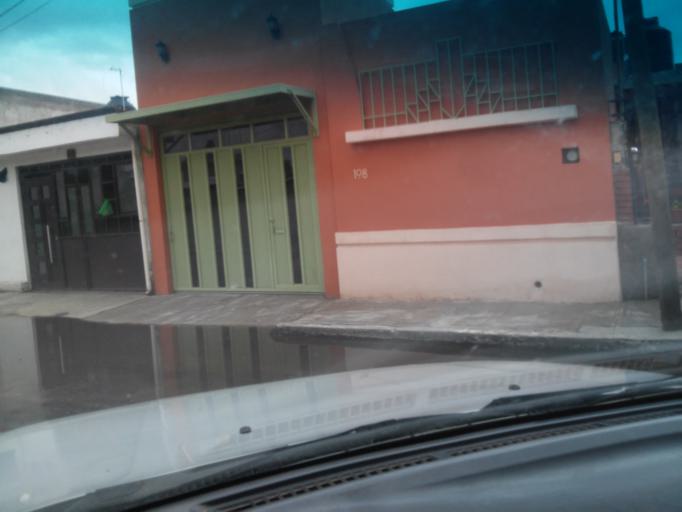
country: MX
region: Durango
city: Victoria de Durango
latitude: 24.0192
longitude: -104.6364
